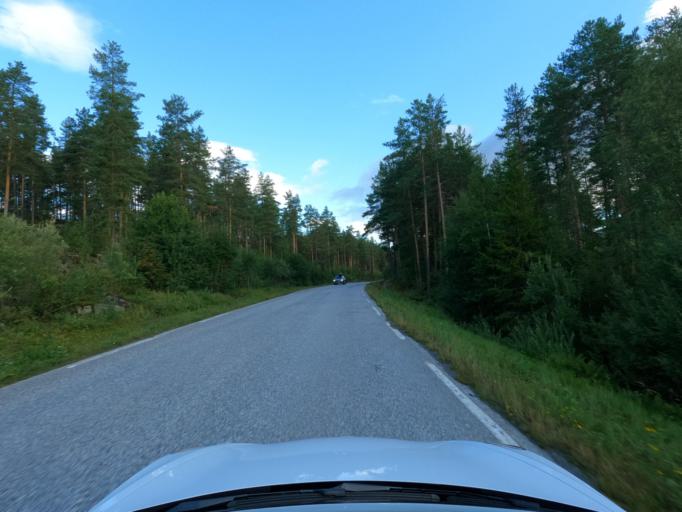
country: NO
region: Telemark
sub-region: Hjartdal
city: Sauland
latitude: 59.8055
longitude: 9.0838
